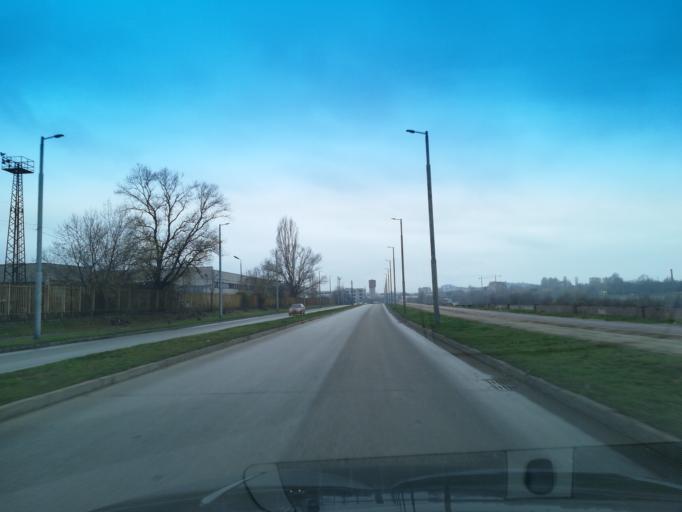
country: BG
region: Plovdiv
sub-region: Obshtina Plovdiv
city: Plovdiv
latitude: 42.1590
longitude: 24.7782
